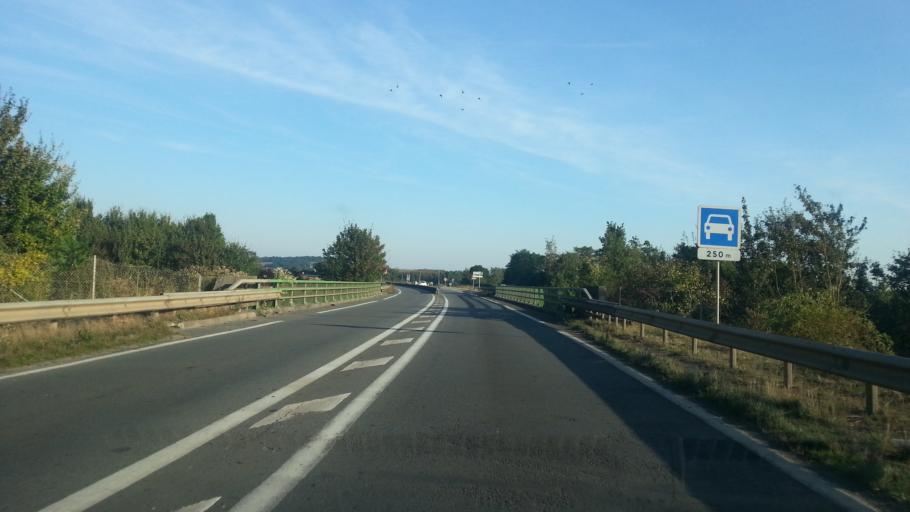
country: FR
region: Picardie
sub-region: Departement de l'Oise
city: Allonne
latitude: 49.4280
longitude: 2.1282
